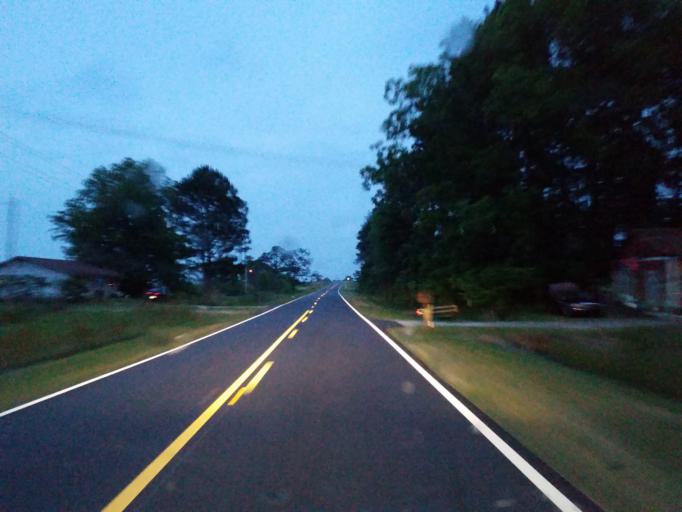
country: US
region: Georgia
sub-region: Tift County
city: Tifton
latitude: 31.5695
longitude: -83.5598
